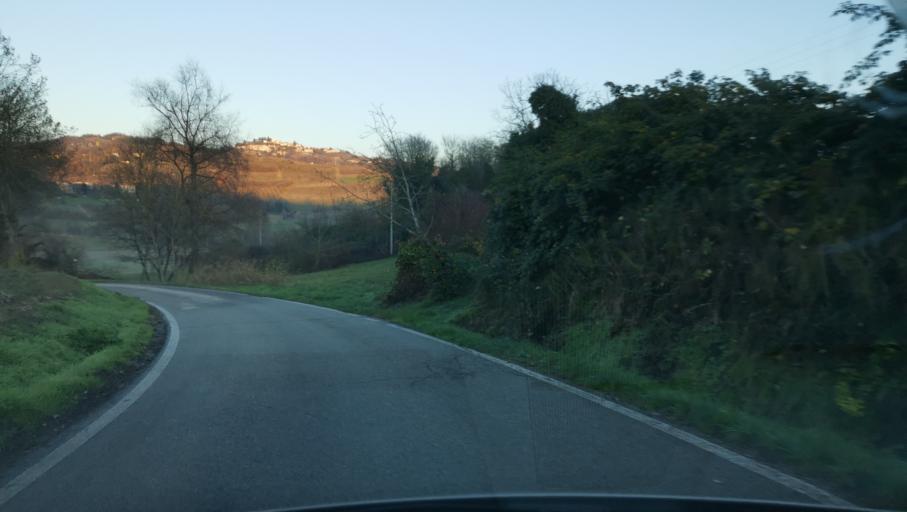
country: IT
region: Piedmont
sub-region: Provincia di Asti
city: Moncucco Torinese
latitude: 45.0638
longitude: 7.9407
